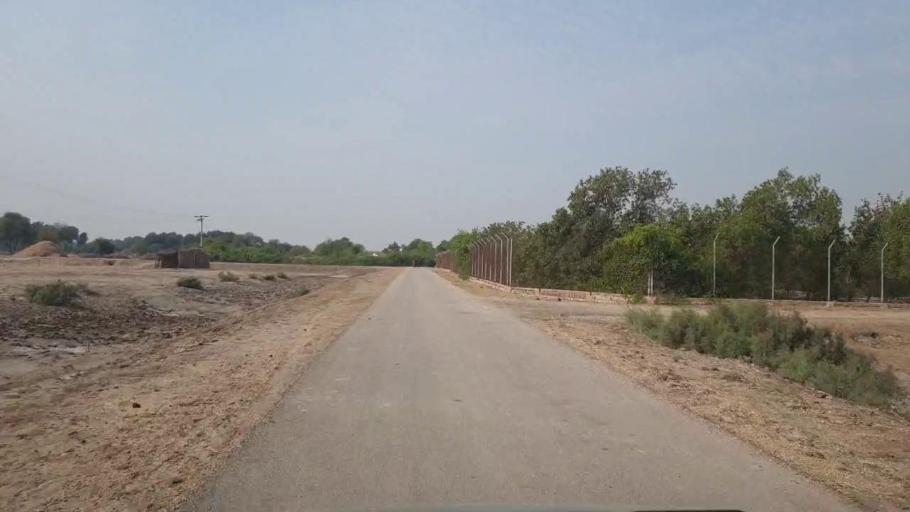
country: PK
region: Sindh
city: Tando Muhammad Khan
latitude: 25.1285
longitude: 68.4545
